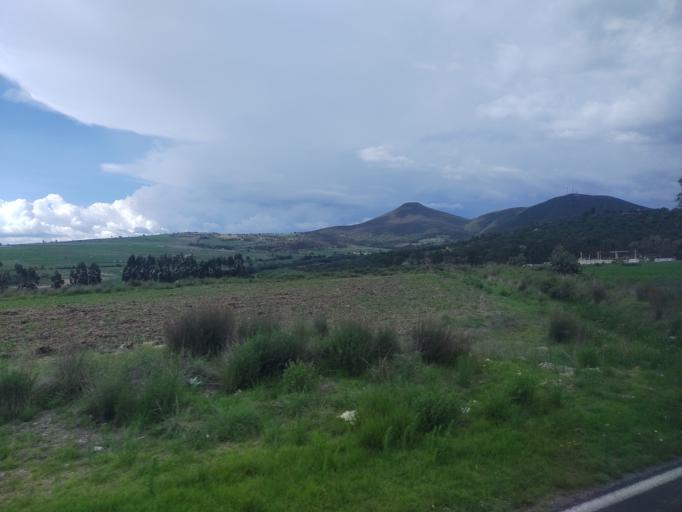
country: MX
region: Mexico
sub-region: Aculco
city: El Colorado
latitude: 20.1035
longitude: -99.7037
